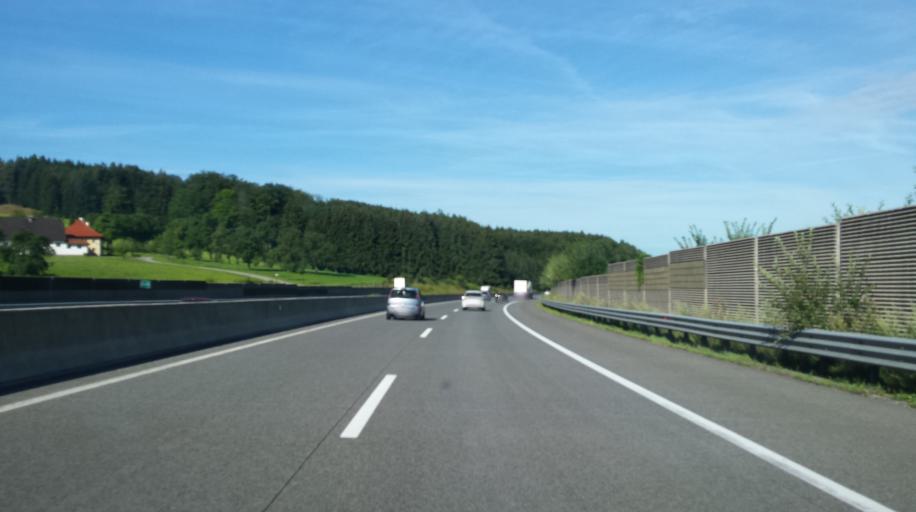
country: AT
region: Upper Austria
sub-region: Politischer Bezirk Vocklabruck
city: Aurach am Hongar
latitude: 47.9504
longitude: 13.7114
